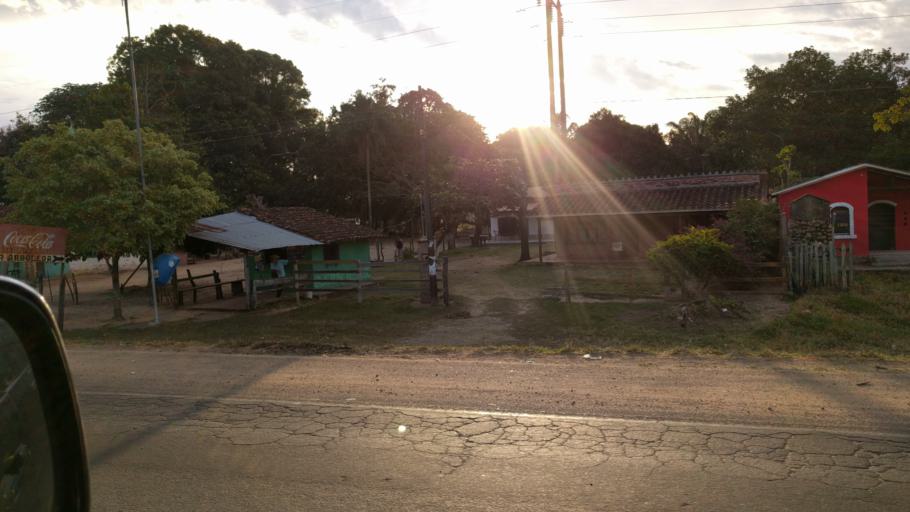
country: BO
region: Santa Cruz
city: Buena Vista
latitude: -17.4083
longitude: -63.6111
